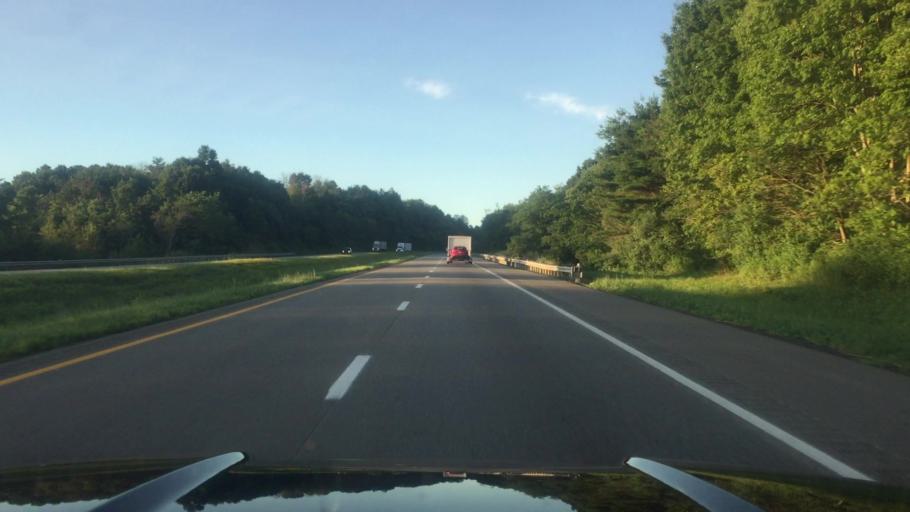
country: US
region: Ohio
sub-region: Tuscarawas County
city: Strasburg
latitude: 40.6055
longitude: -81.5001
